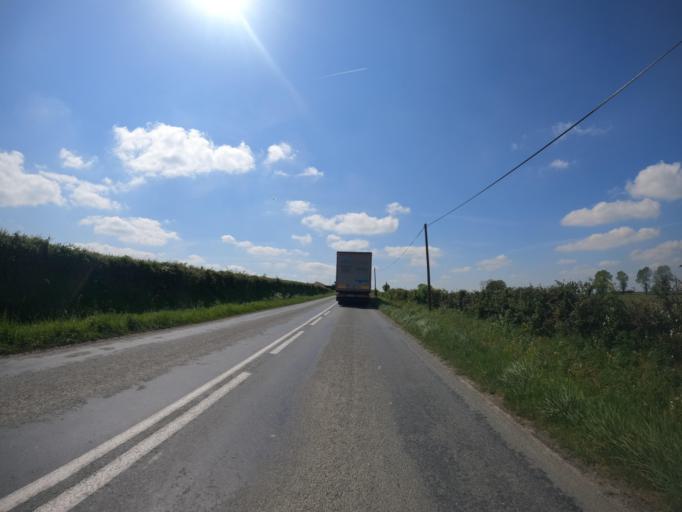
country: FR
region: Poitou-Charentes
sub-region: Departement des Deux-Sevres
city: Boisme
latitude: 46.7196
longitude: -0.3941
